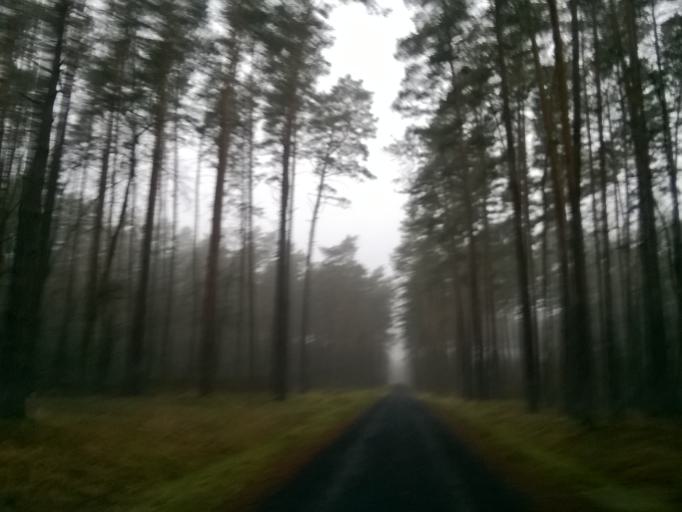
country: PL
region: Kujawsko-Pomorskie
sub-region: Powiat nakielski
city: Kcynia
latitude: 53.0426
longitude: 17.5123
